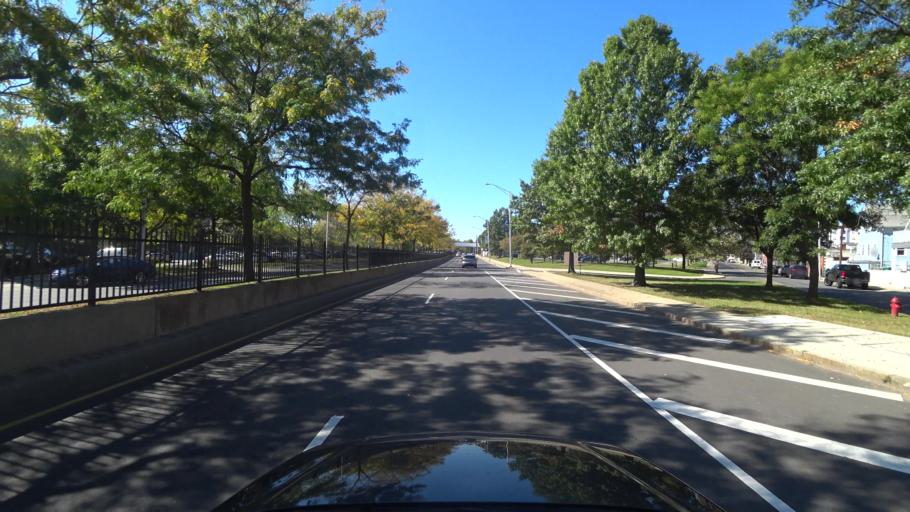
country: US
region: Massachusetts
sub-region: Essex County
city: Lynn
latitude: 42.4588
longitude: -70.9405
